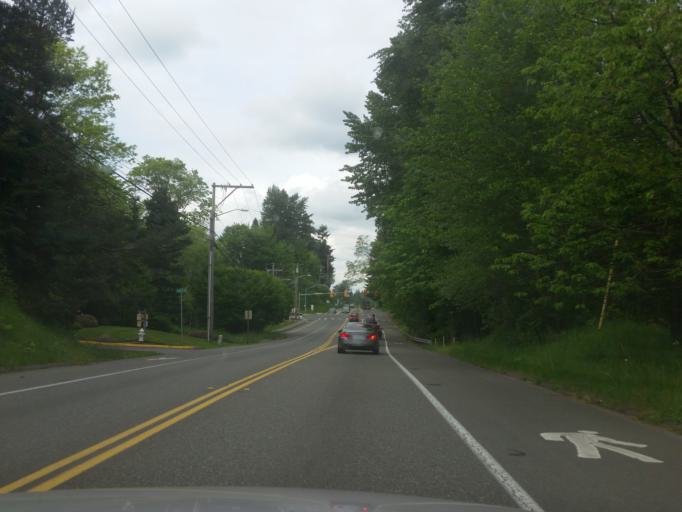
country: US
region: Washington
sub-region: King County
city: Inglewood-Finn Hill
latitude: 47.7292
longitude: -122.2078
